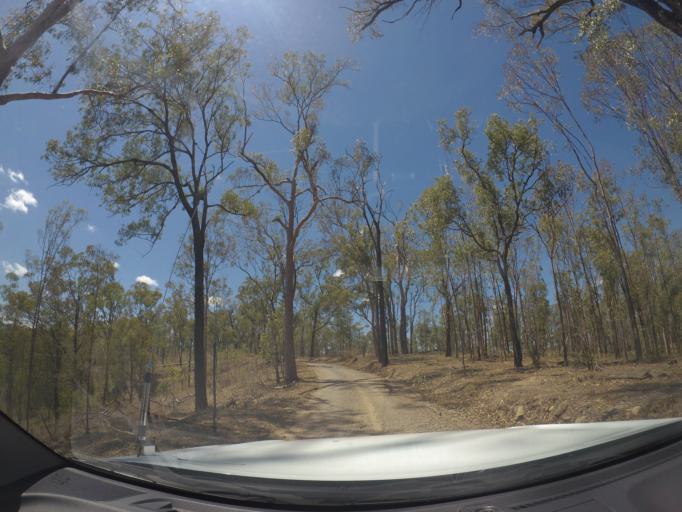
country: AU
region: Queensland
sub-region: Ipswich
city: Deebing Heights
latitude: -27.8292
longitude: 152.8326
